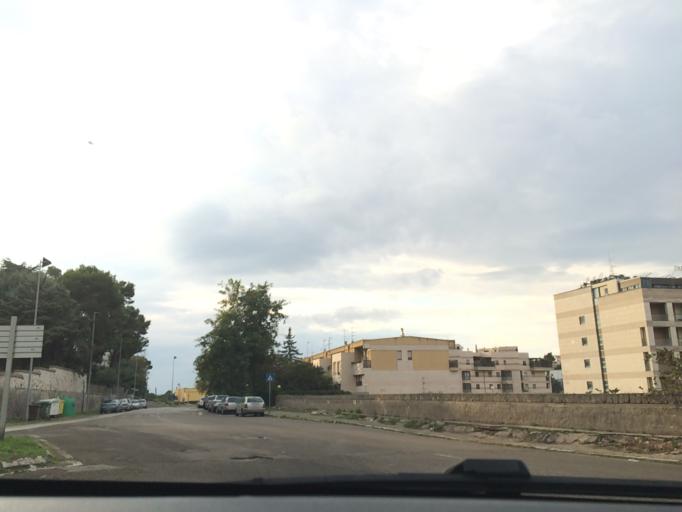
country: IT
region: Basilicate
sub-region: Provincia di Matera
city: Matera
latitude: 40.6628
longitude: 16.5990
